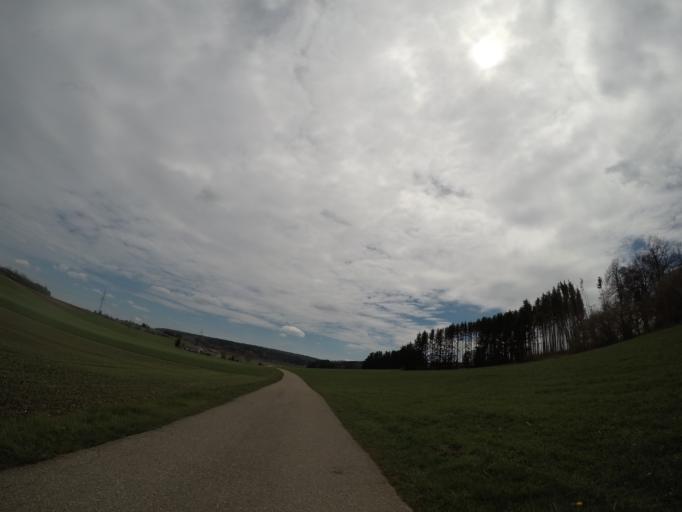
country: DE
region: Baden-Wuerttemberg
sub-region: Tuebingen Region
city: Westerheim
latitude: 48.5030
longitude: 9.6464
